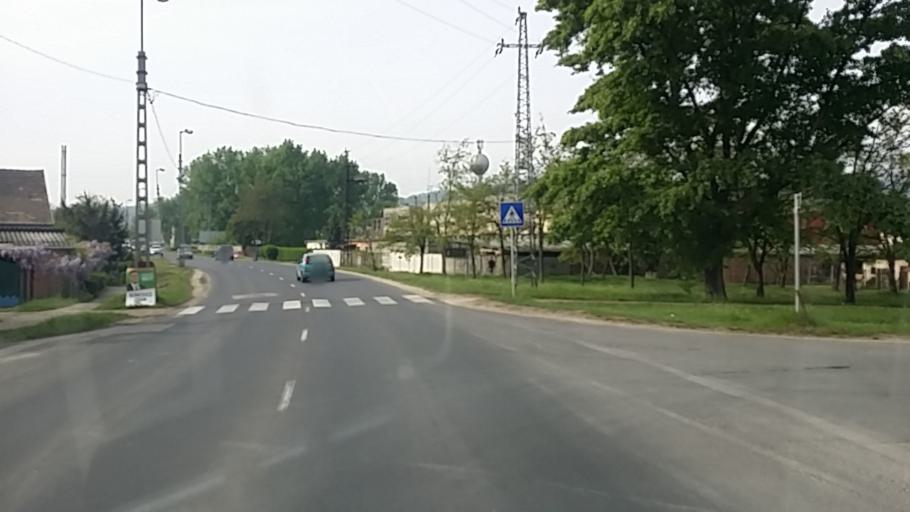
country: HU
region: Komarom-Esztergom
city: Dorog
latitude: 47.7350
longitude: 18.7249
